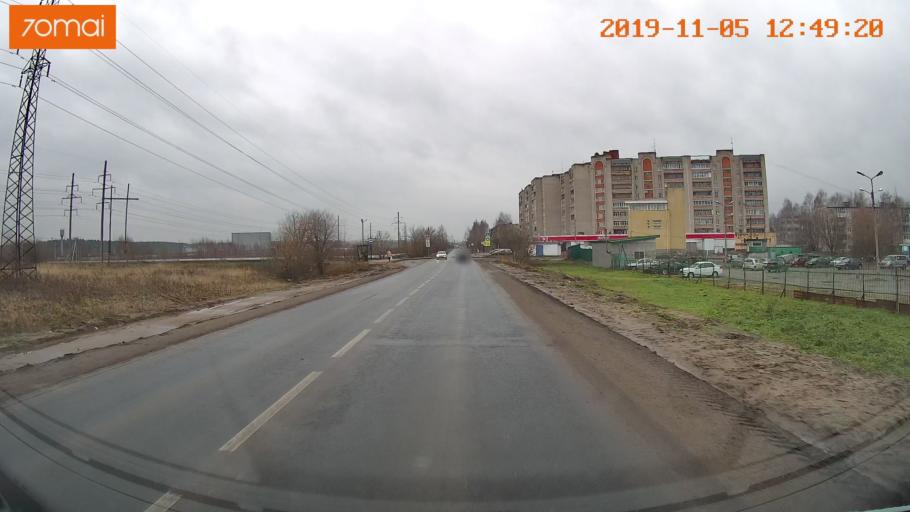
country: RU
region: Ivanovo
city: Kokhma
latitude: 56.9552
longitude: 41.1036
